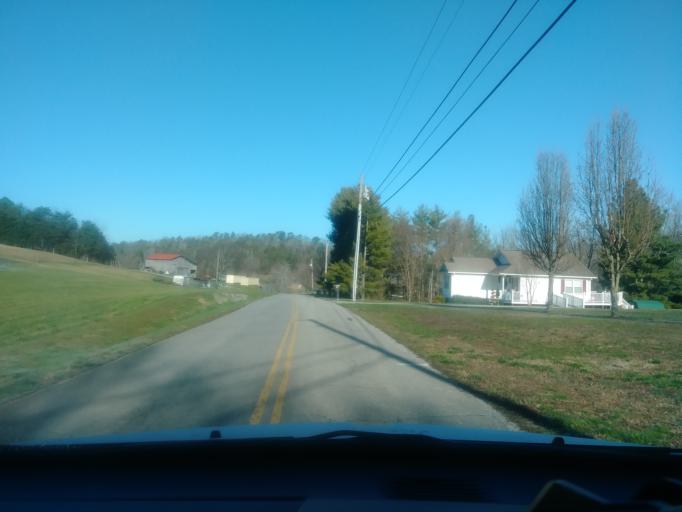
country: US
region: Tennessee
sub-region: Greene County
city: Mosheim
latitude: 36.1105
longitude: -82.9298
